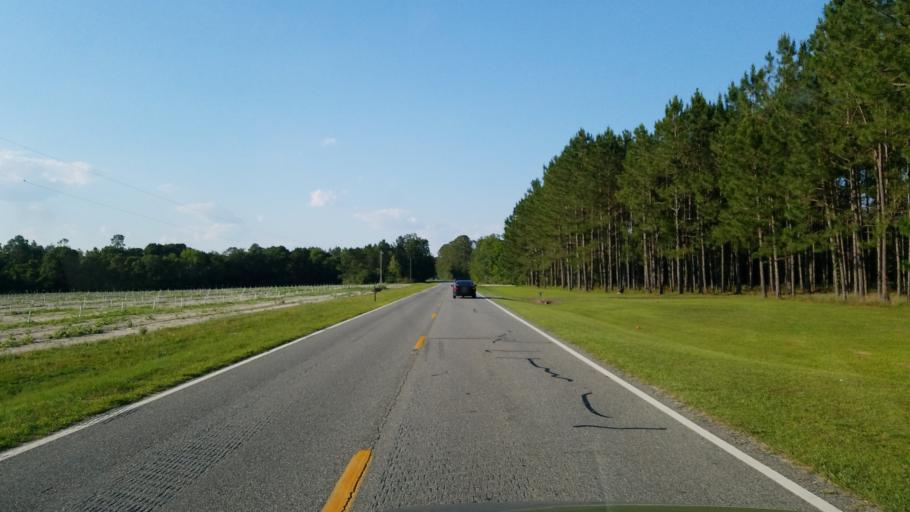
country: US
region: Georgia
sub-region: Lanier County
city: Lakeland
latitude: 30.9882
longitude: -83.0713
